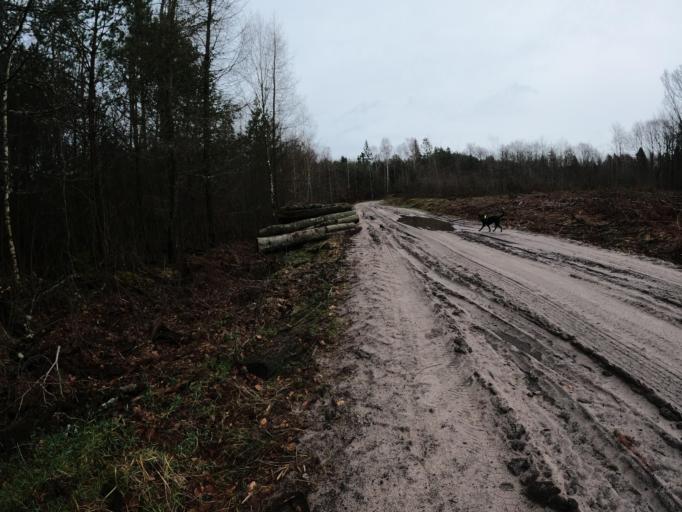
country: PL
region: West Pomeranian Voivodeship
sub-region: Powiat slawienski
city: Darlowo
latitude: 54.3921
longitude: 16.4817
